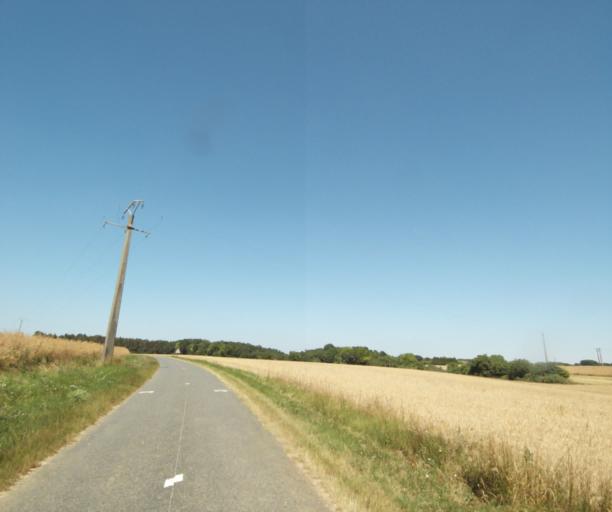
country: FR
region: Ile-de-France
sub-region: Departement de Seine-et-Marne
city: Noisy-sur-Ecole
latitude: 48.3084
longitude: 2.5000
